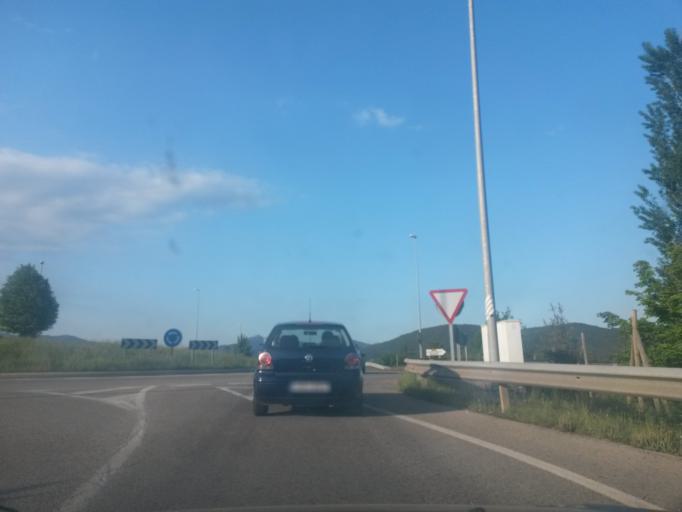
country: ES
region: Catalonia
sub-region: Provincia de Girona
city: Sant Joan les Fonts
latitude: 42.1934
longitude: 2.5257
